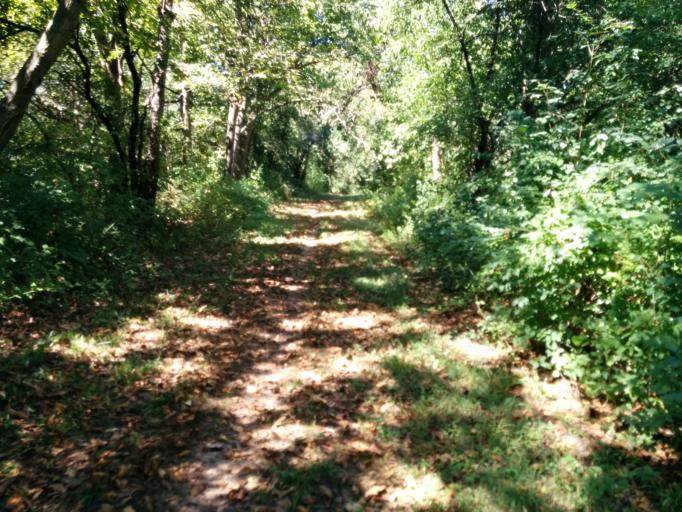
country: US
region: Illinois
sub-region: Cook County
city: Western Springs
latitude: 41.8202
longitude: -87.9125
